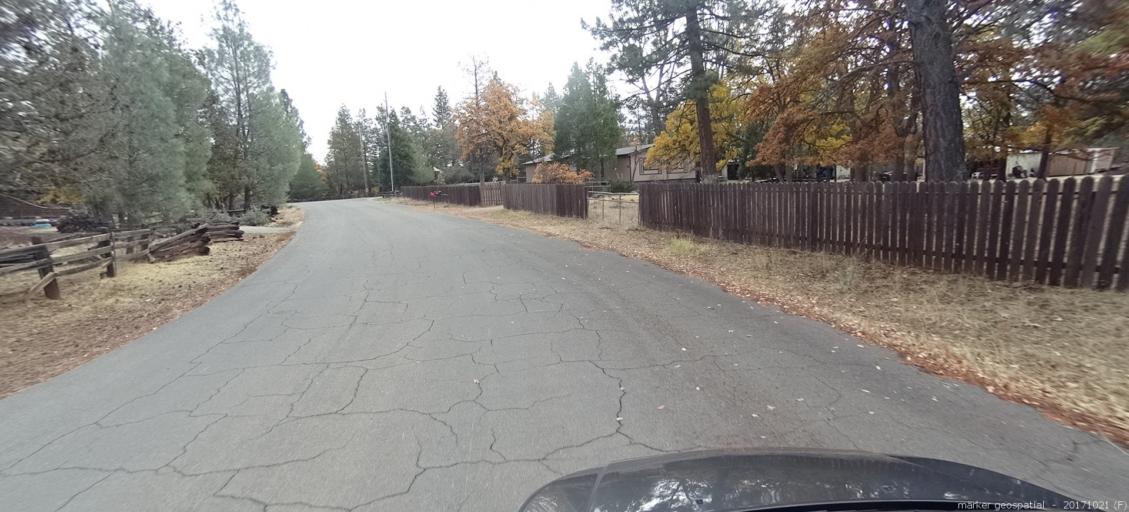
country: US
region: California
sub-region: Shasta County
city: Burney
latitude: 40.9146
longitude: -121.5557
